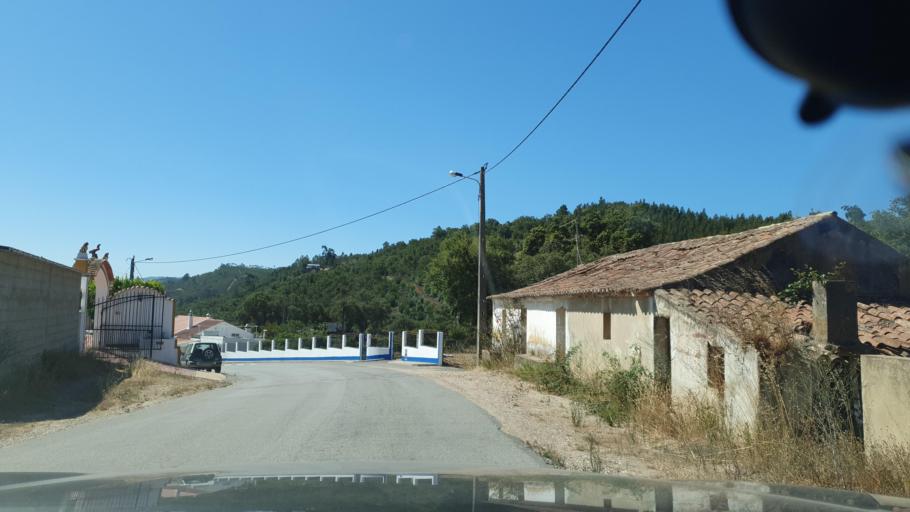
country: PT
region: Beja
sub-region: Odemira
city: Sao Teotonio
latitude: 37.5004
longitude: -8.6548
